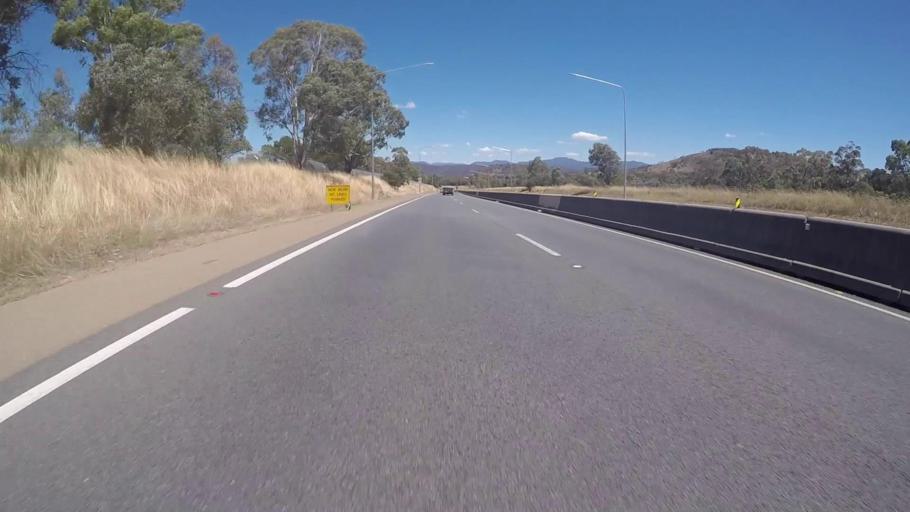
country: AU
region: Australian Capital Territory
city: Macarthur
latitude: -35.3675
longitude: 149.0620
